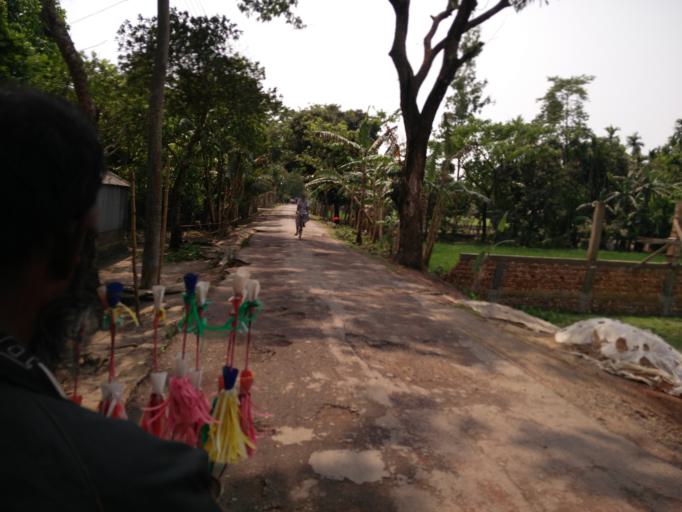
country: BD
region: Dhaka
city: Sherpur
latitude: 24.9543
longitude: 90.1675
